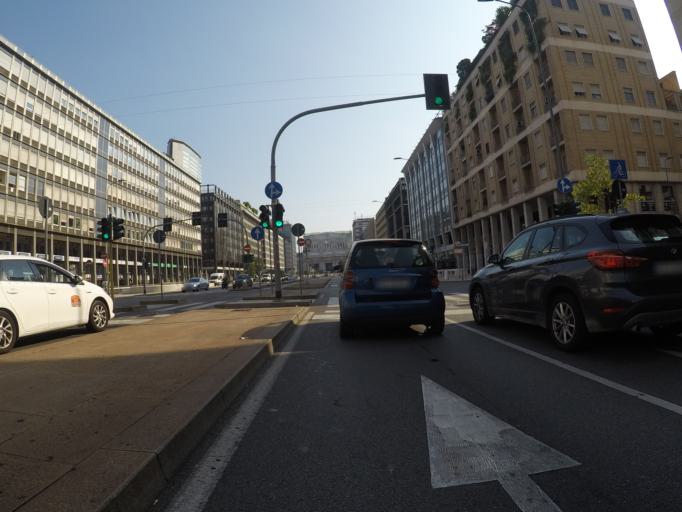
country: IT
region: Lombardy
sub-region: Citta metropolitana di Milano
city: Milano
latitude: 45.4815
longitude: 9.2000
